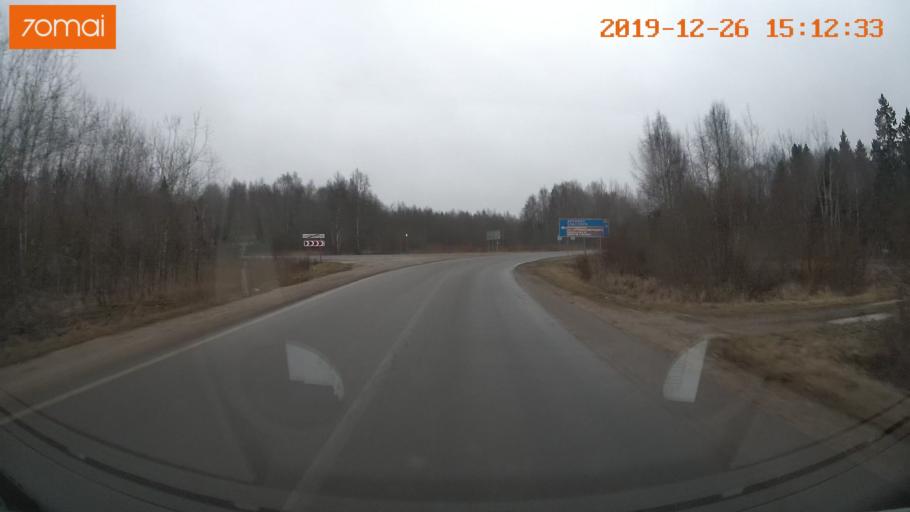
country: RU
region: Jaroslavl
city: Rybinsk
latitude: 58.1268
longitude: 38.8779
